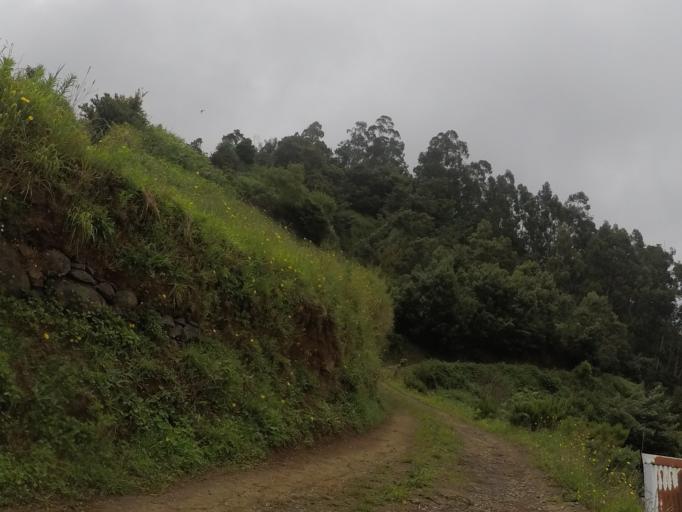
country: PT
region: Madeira
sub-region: Santana
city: Santana
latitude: 32.7745
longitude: -16.8773
